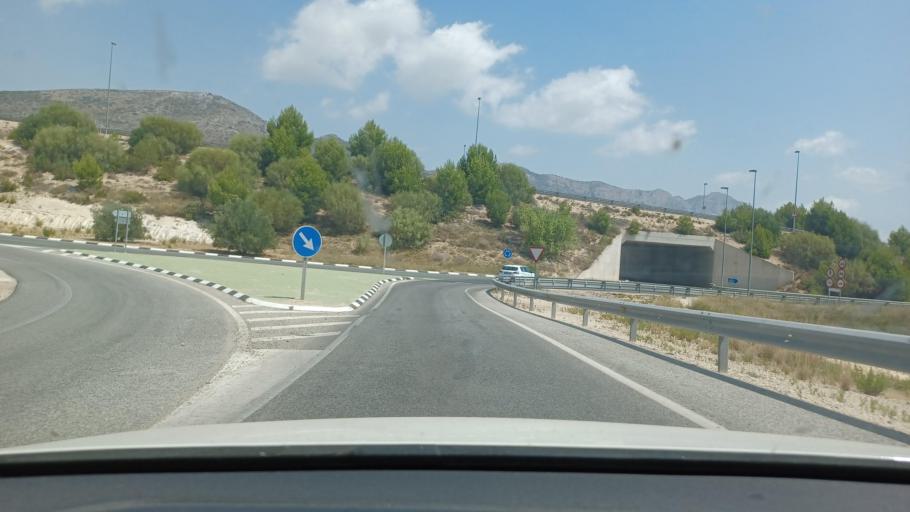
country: ES
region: Valencia
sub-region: Provincia de Alicante
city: Muro del Alcoy
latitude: 38.7933
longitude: -0.4495
